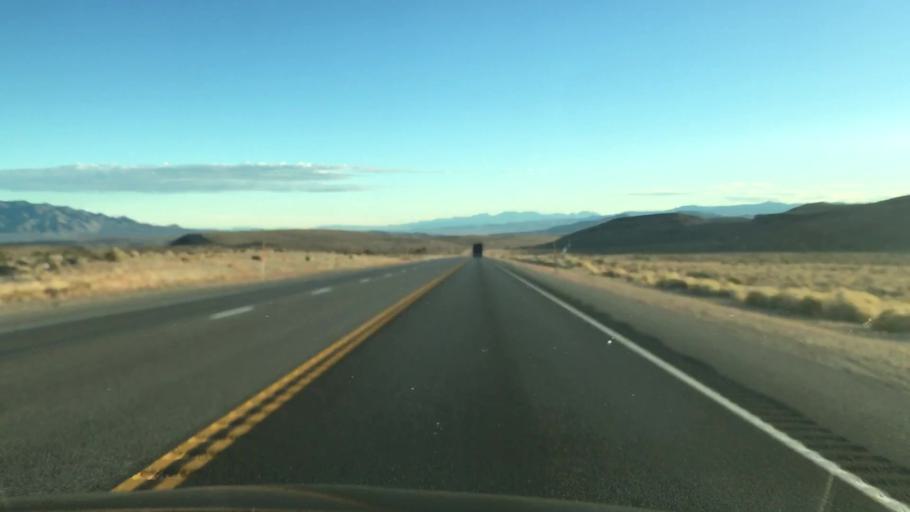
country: US
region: Nevada
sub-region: Esmeralda County
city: Goldfield
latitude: 37.6665
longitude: -117.2185
